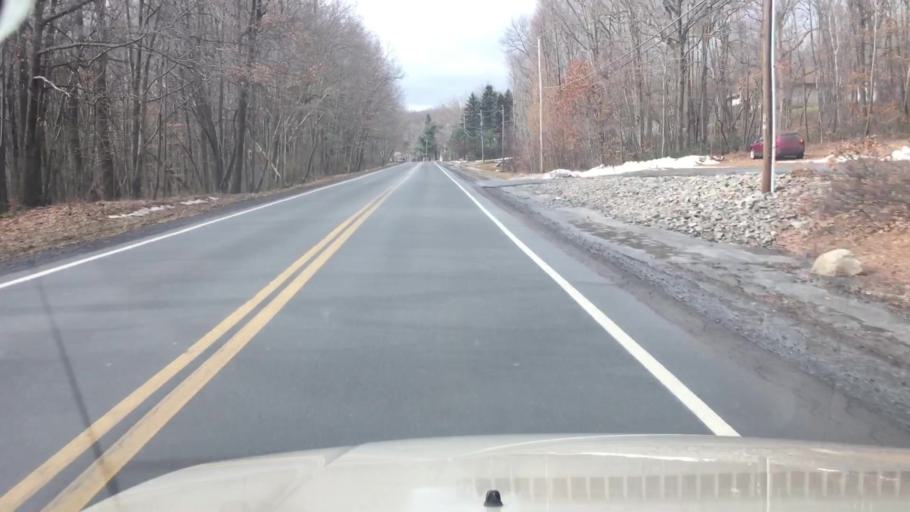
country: US
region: Pennsylvania
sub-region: Luzerne County
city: Harleigh
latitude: 40.9863
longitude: -75.9487
